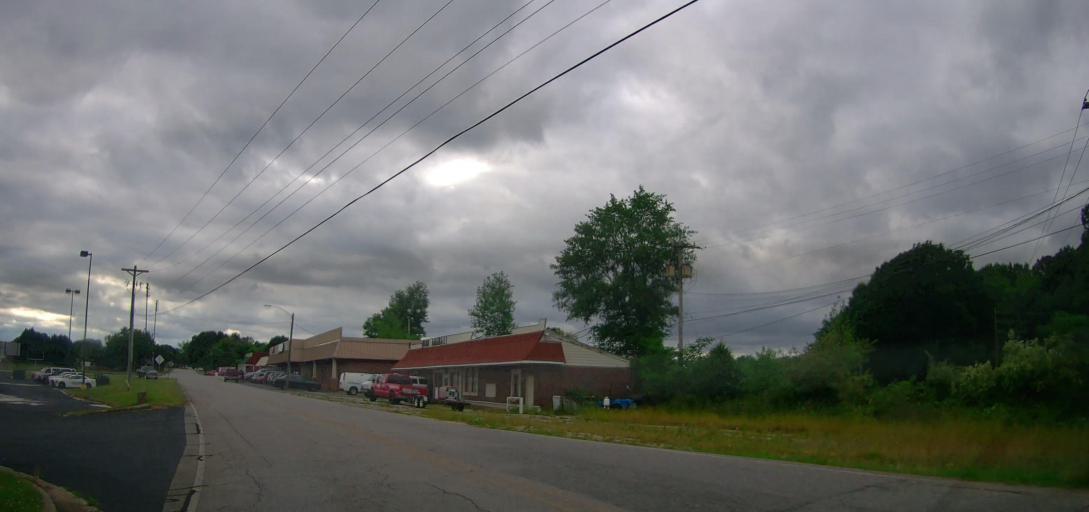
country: US
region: Georgia
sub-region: Walton County
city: Monroe
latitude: 33.8040
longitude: -83.7014
